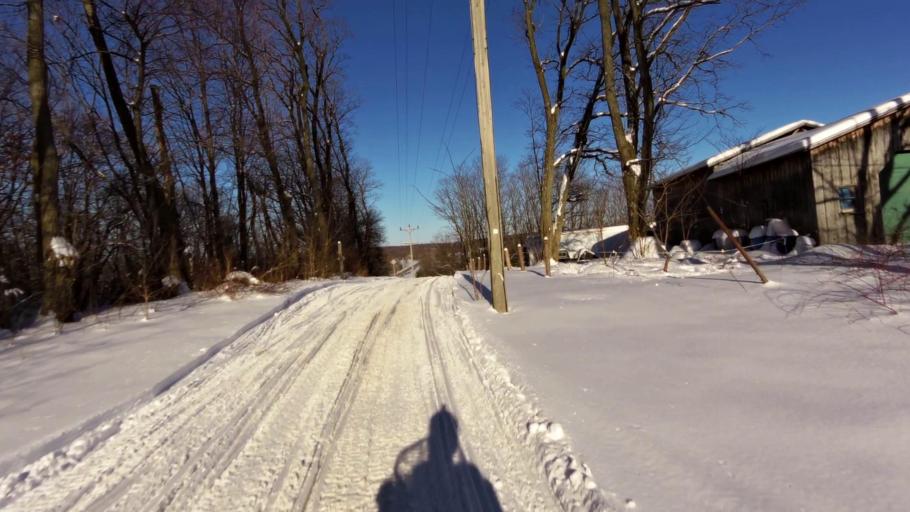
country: US
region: New York
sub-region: Chautauqua County
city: Mayville
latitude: 42.2818
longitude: -79.4399
